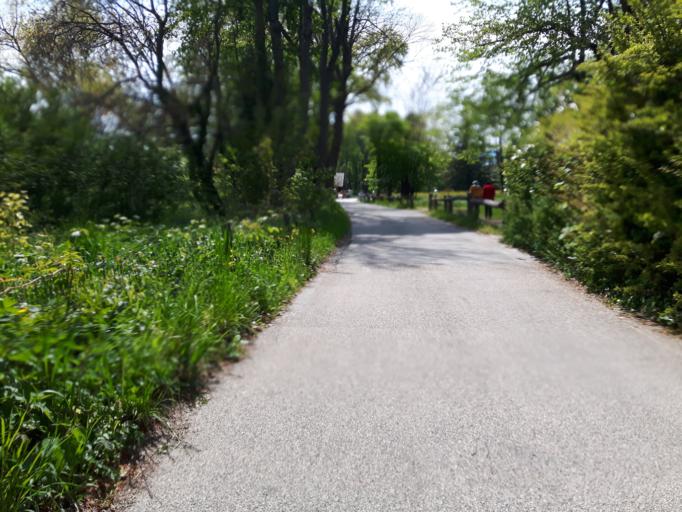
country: CH
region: Neuchatel
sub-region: Boudry District
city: Bevaix
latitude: 46.9231
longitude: 6.8191
